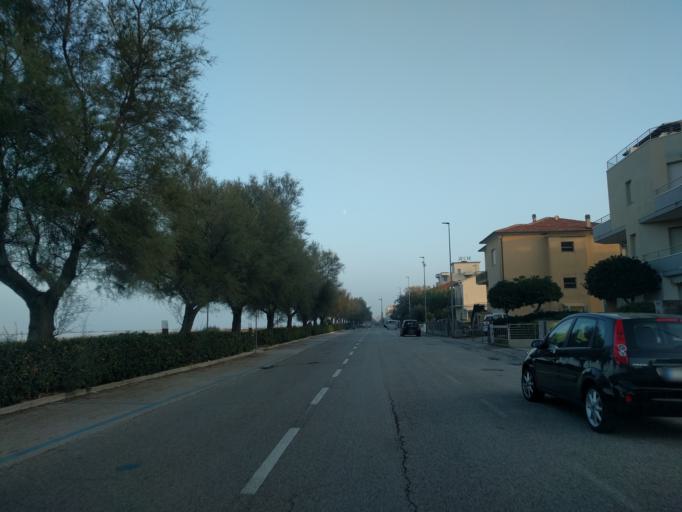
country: IT
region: The Marches
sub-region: Provincia di Ancona
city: Senigallia
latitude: 43.7374
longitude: 13.1906
